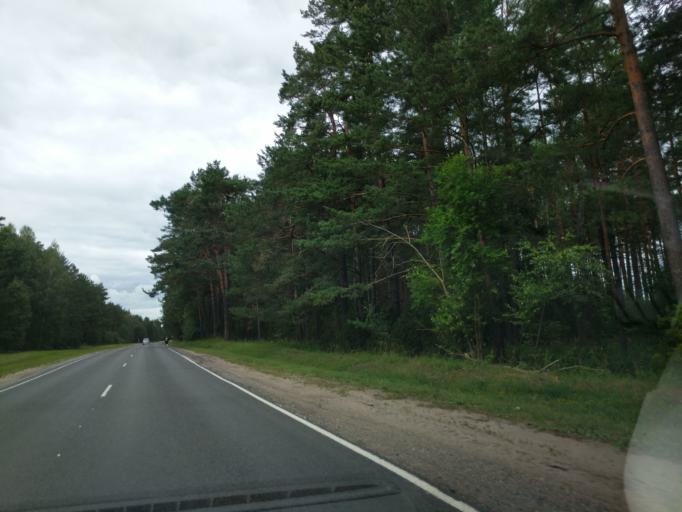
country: BY
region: Minsk
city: Myadzyel
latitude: 54.8372
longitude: 26.9335
